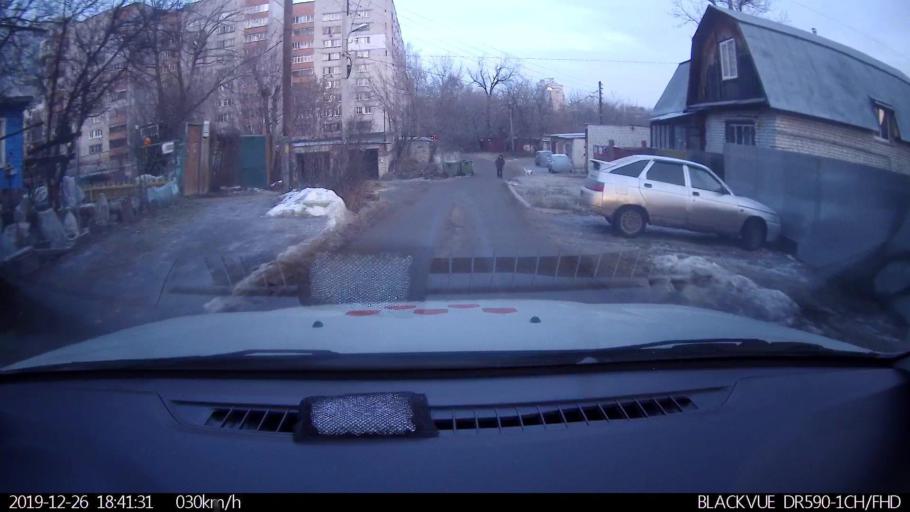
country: RU
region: Nizjnij Novgorod
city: Nizhniy Novgorod
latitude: 56.3160
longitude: 44.0348
